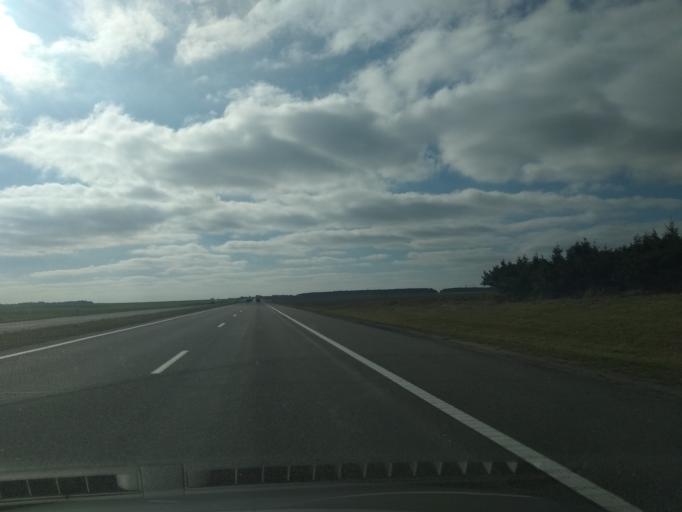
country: BY
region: Grodnenskaya
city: Mir
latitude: 53.4358
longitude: 26.5876
